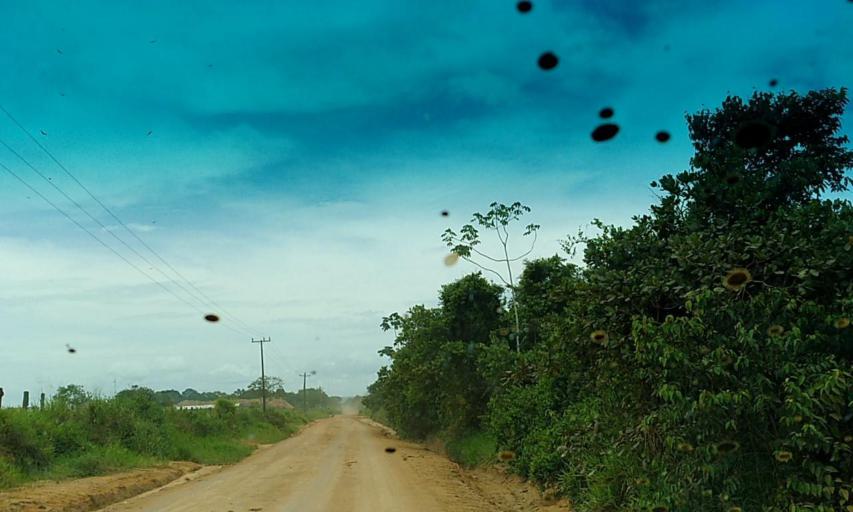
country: BR
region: Para
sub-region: Senador Jose Porfirio
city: Senador Jose Porfirio
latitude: -2.5824
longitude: -51.9337
